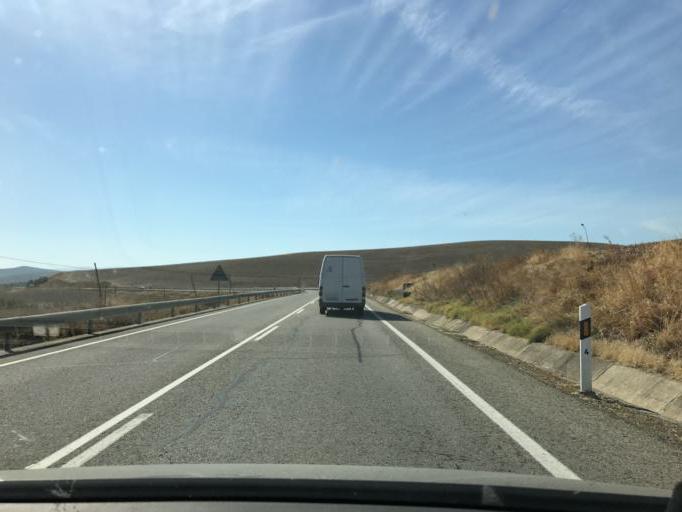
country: ES
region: Andalusia
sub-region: Province of Cordoba
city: Espejo
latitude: 37.7143
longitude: -4.6291
